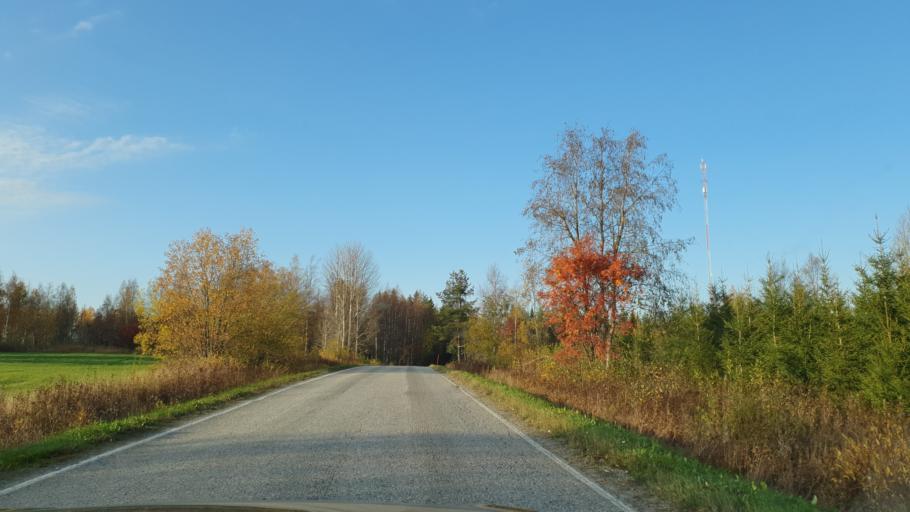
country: FI
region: Kainuu
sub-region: Kehys-Kainuu
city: Kuhmo
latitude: 64.2078
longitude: 29.4463
